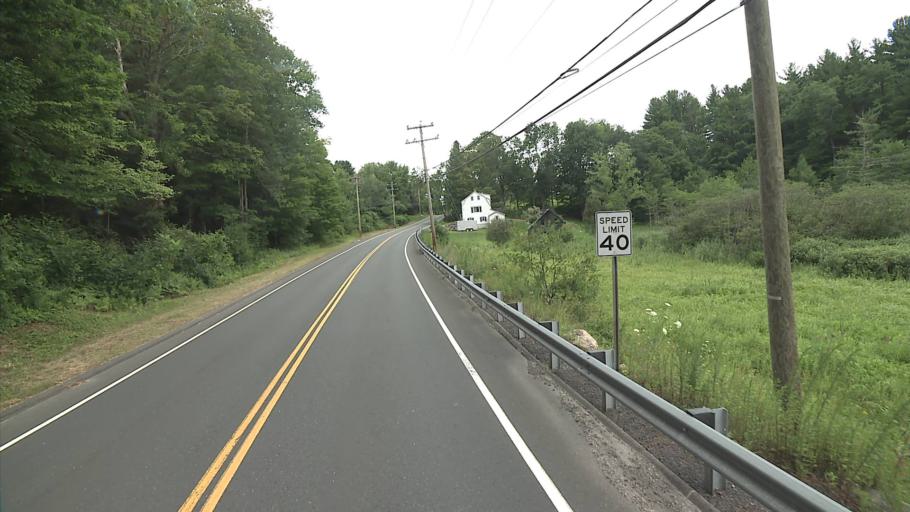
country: US
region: Connecticut
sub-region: Litchfield County
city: Winsted
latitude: 41.9590
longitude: -73.0491
